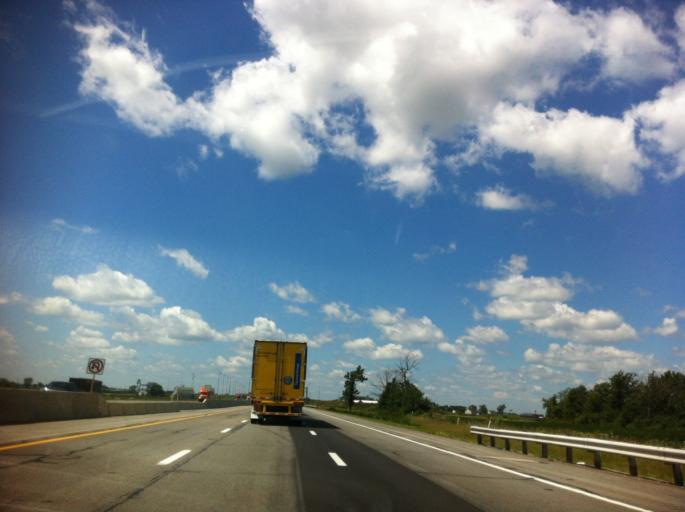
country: US
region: Ohio
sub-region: Wood County
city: Millbury
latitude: 41.5185
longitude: -83.4433
